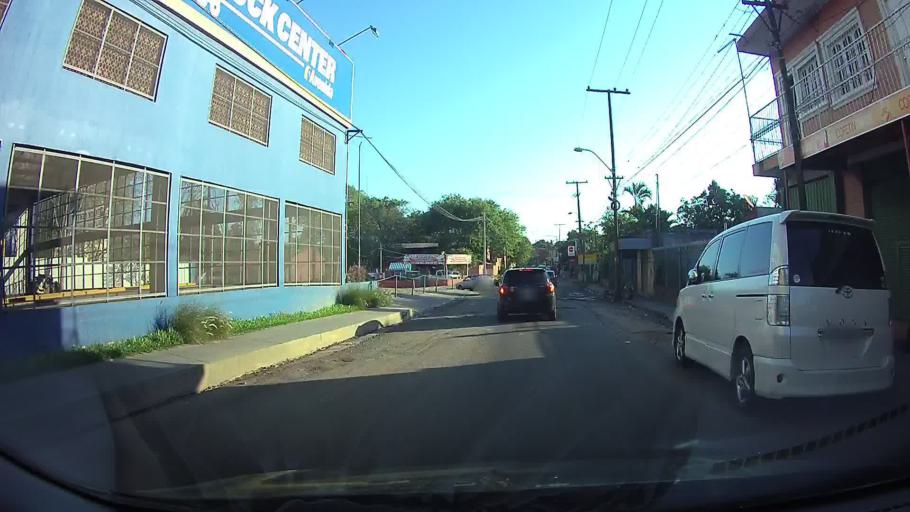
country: PY
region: Central
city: Fernando de la Mora
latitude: -25.3372
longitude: -57.5292
